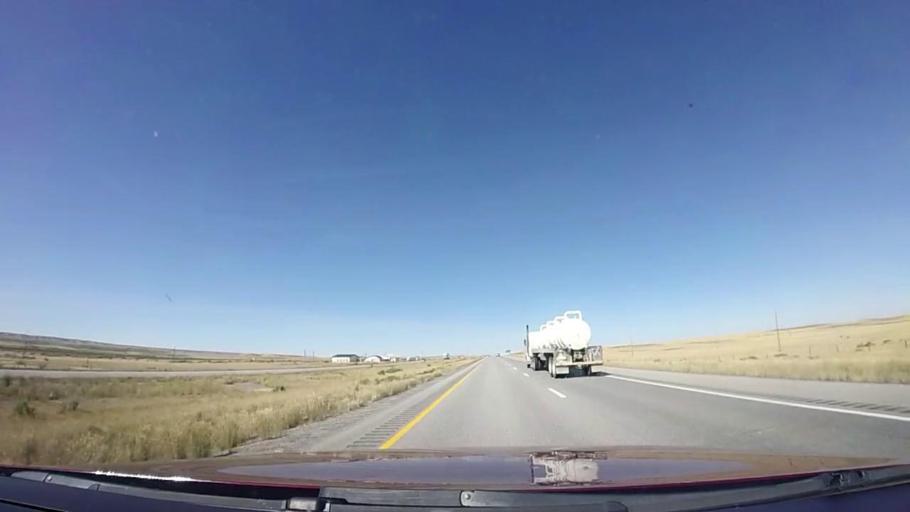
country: US
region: Wyoming
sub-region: Carbon County
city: Rawlins
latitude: 41.6545
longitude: -108.1136
